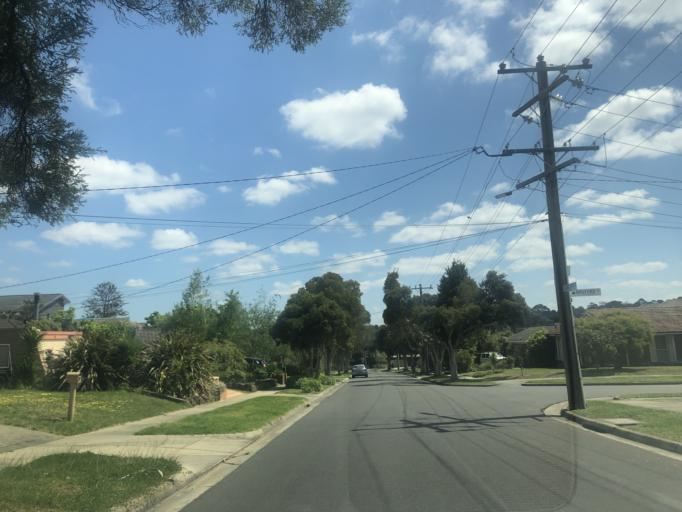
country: AU
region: Victoria
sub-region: Monash
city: Mulgrave
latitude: -37.9133
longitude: 145.1868
